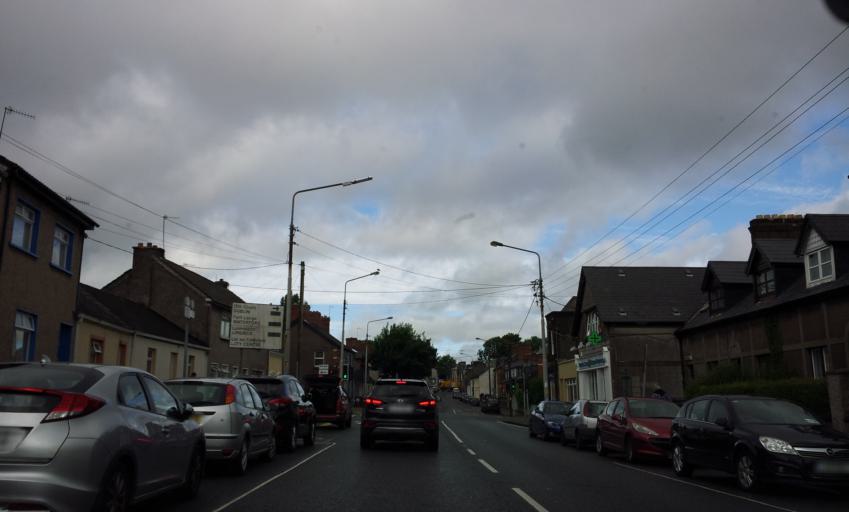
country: IE
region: Munster
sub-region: County Cork
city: Cork
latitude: 51.8891
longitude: -8.4690
